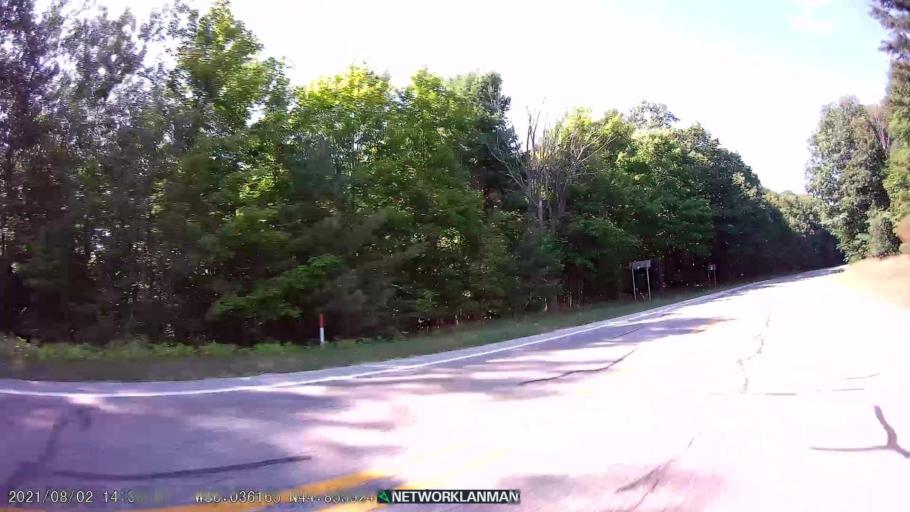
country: US
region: Michigan
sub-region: Benzie County
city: Beulah
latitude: 44.8563
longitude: -86.0361
